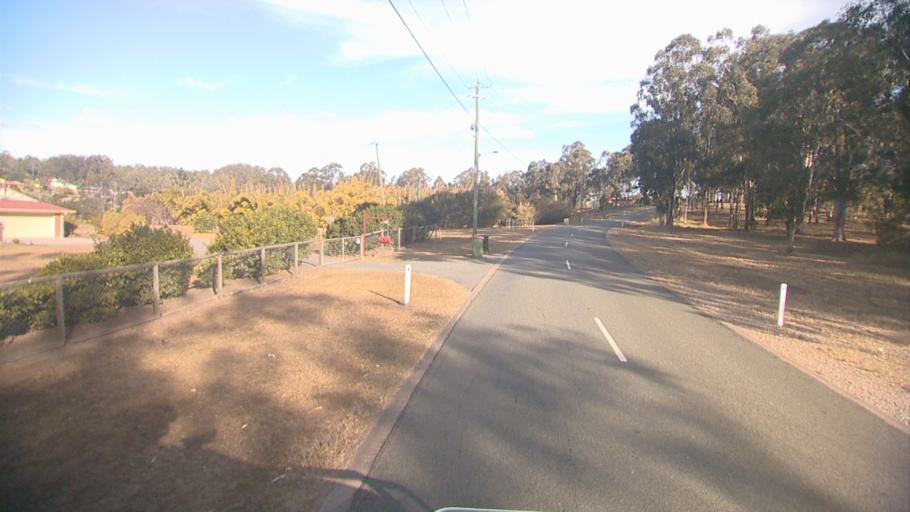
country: AU
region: Queensland
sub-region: Logan
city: Cedar Vale
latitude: -27.8811
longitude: 153.0106
